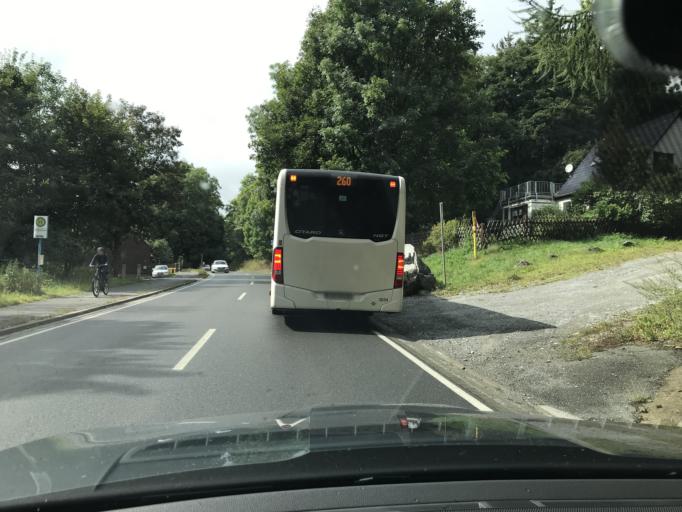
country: DE
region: Saxony-Anhalt
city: Elbingerode
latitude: 51.7679
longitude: 10.8174
